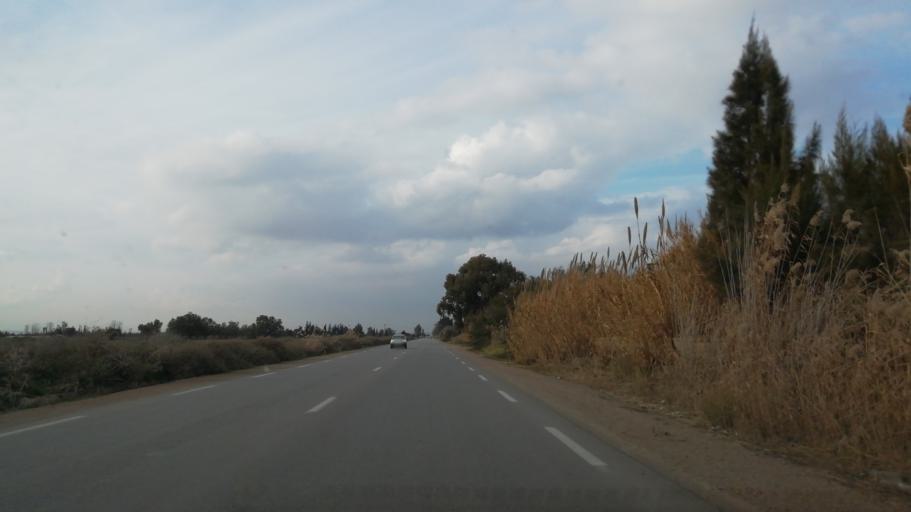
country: DZ
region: Mascara
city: Sig
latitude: 35.6745
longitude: -0.0057
